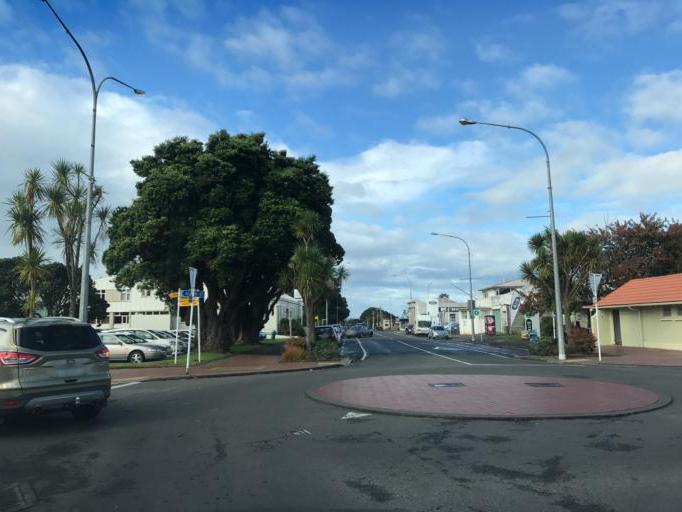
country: NZ
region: Taranaki
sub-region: South Taranaki District
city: Hawera
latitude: -39.5896
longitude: 174.2847
